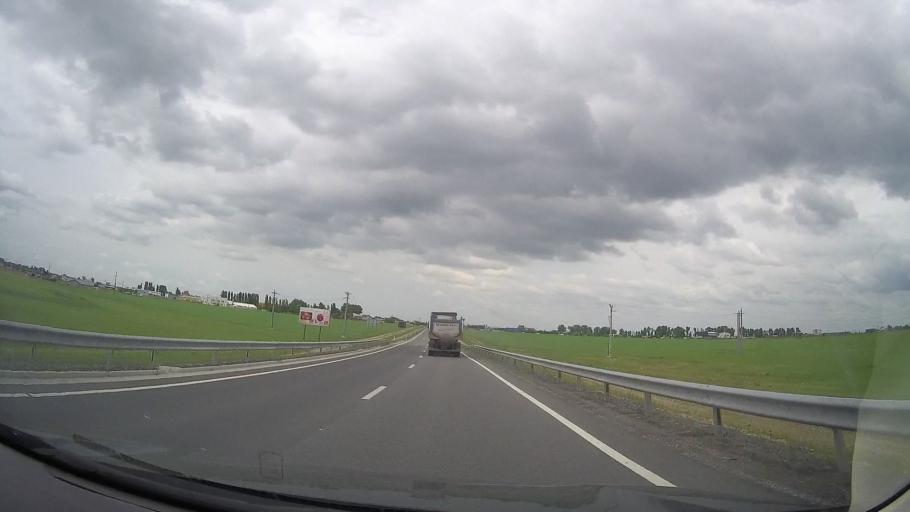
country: RO
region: Dolj
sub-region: Comuna Carcea
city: Carcea
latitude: 44.3086
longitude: 23.9135
